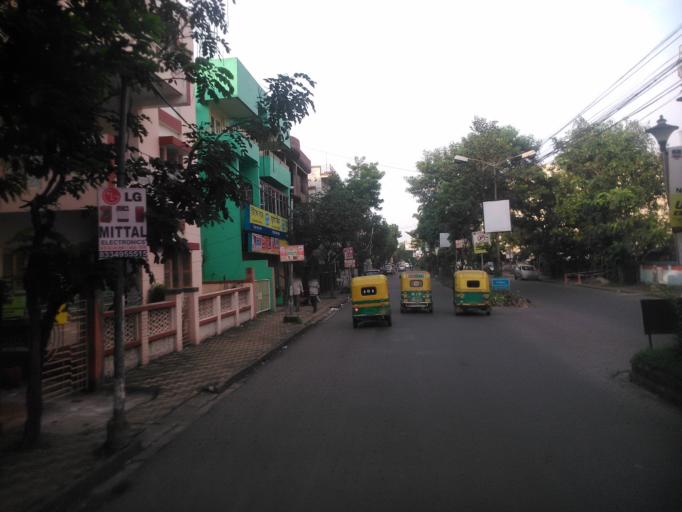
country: IN
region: West Bengal
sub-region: North 24 Parganas
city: Garui
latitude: 22.5921
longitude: 88.4005
